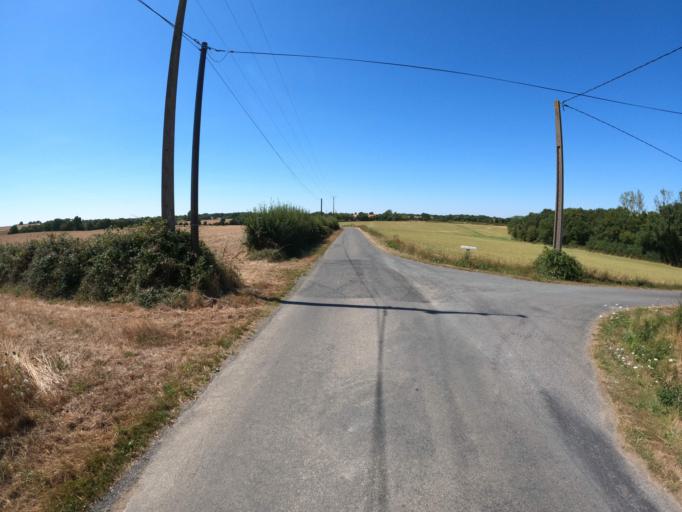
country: FR
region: Pays de la Loire
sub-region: Departement de Maine-et-Loire
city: Saint-Christophe-du-Bois
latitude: 47.0466
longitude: -0.9581
